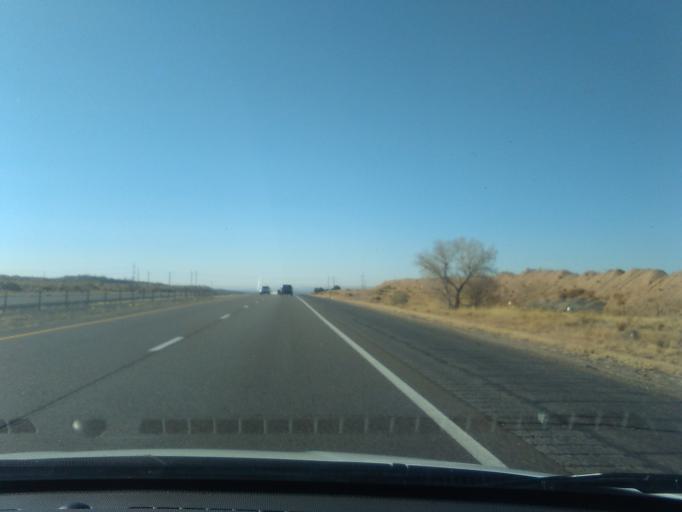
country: US
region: New Mexico
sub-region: Sandoval County
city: Bernalillo
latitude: 35.3584
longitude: -106.4945
